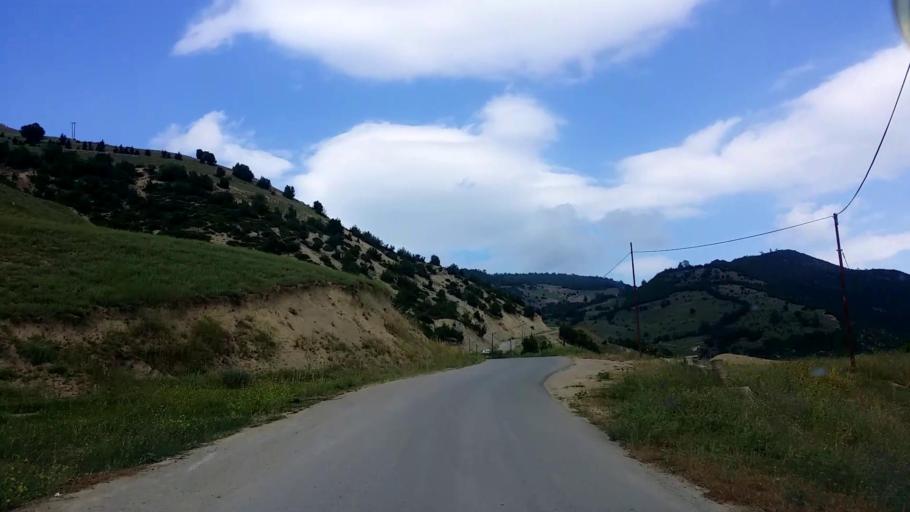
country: IR
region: Mazandaran
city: Chalus
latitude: 36.5526
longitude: 51.2847
